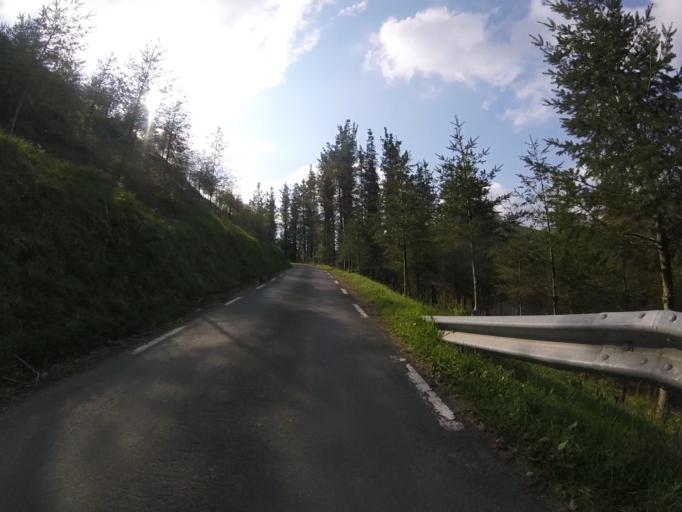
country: ES
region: Basque Country
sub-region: Provincia de Guipuzcoa
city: Azkoitia
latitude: 43.2243
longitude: -2.3167
